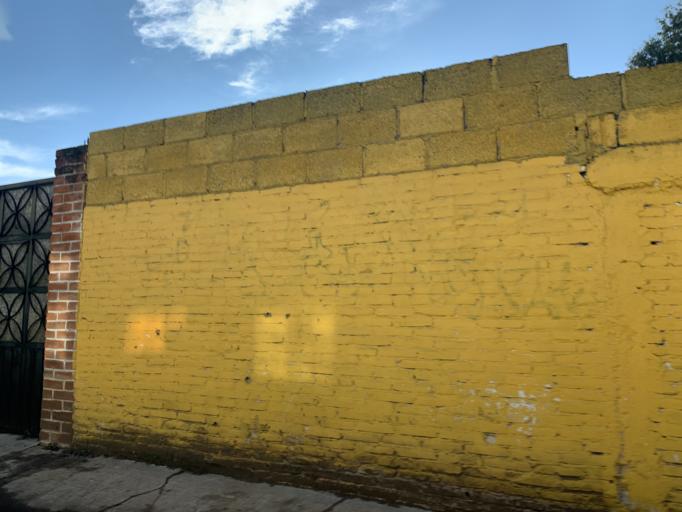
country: MX
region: Puebla
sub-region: Cuautlancingo
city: Sanctorum
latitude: 19.0777
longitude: -98.2423
